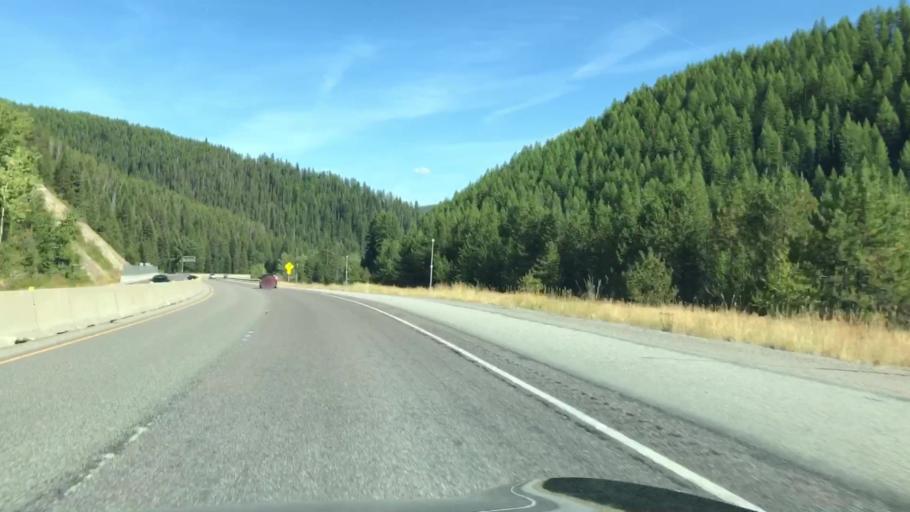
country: US
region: Montana
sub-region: Sanders County
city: Thompson Falls
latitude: 47.4187
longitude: -115.5989
